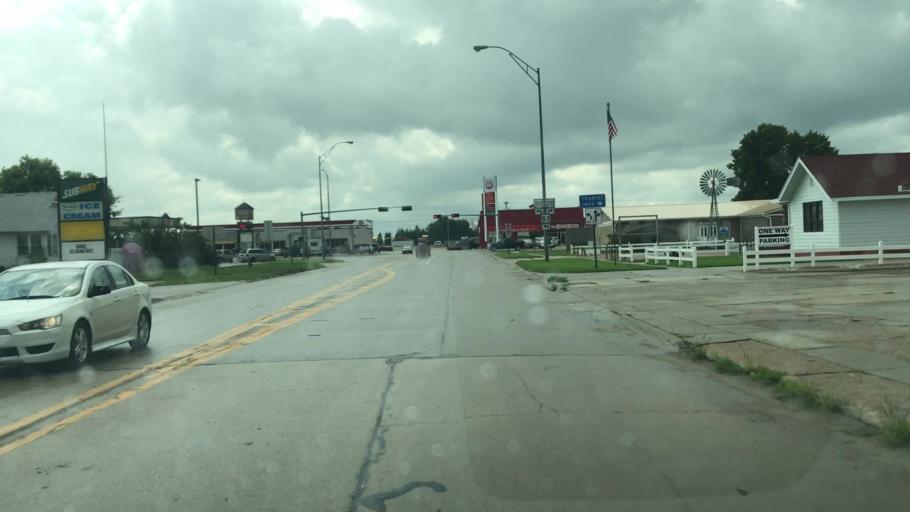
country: US
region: Nebraska
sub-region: Cherry County
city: Valentine
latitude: 42.8690
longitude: -100.5505
